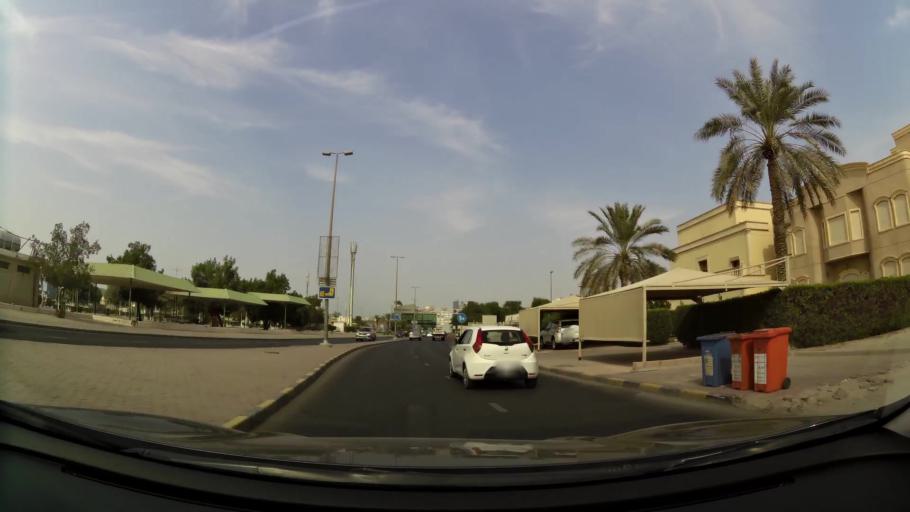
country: KW
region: Al Asimah
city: Ash Shamiyah
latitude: 29.3370
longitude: 47.9620
